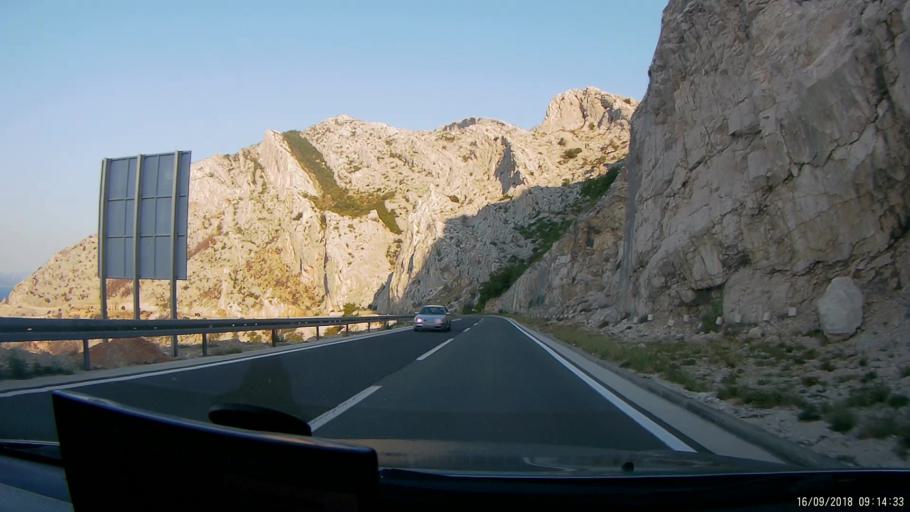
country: HR
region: Splitsko-Dalmatinska
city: Donja Brela
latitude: 43.4034
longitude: 16.8894
